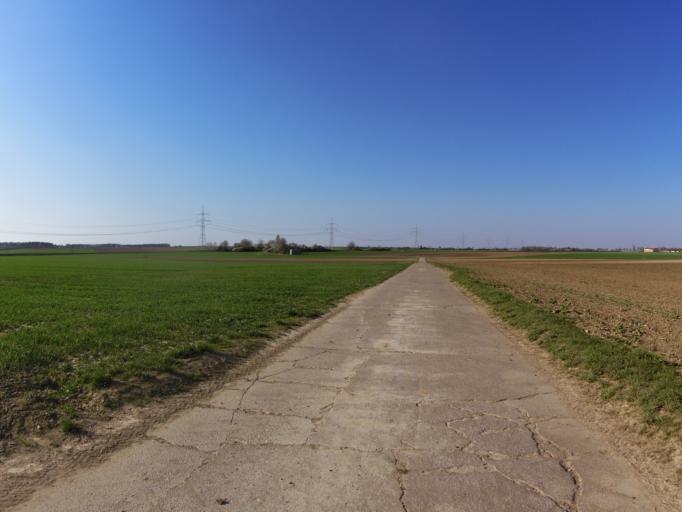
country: DE
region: Bavaria
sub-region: Regierungsbezirk Unterfranken
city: Oberpleichfeld
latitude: 49.8300
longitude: 10.0961
